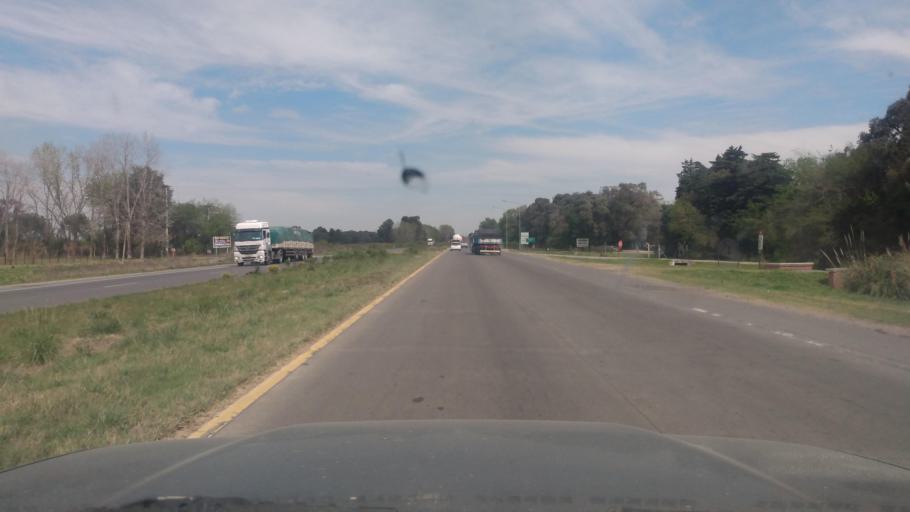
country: AR
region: Buenos Aires
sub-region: Partido de Pilar
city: Pilar
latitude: -34.4388
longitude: -59.0469
